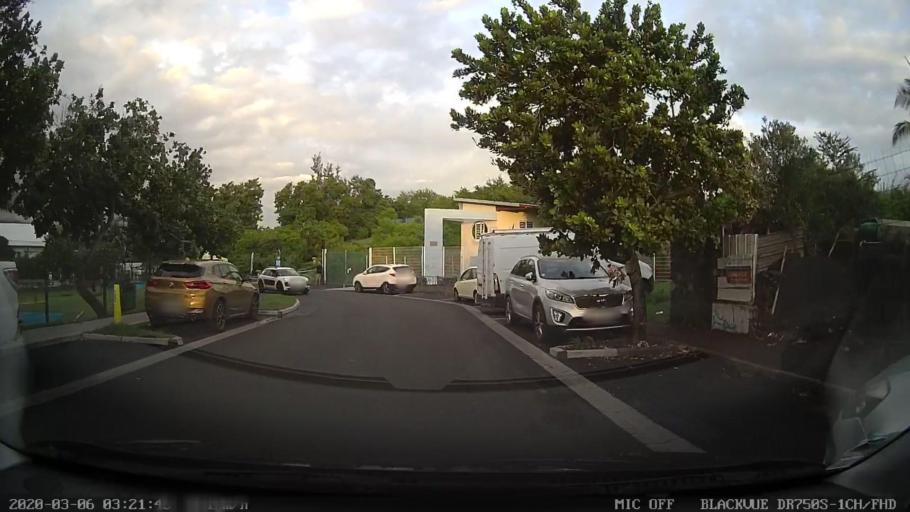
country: RE
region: Reunion
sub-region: Reunion
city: Les Avirons
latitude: -21.2726
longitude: 55.3366
